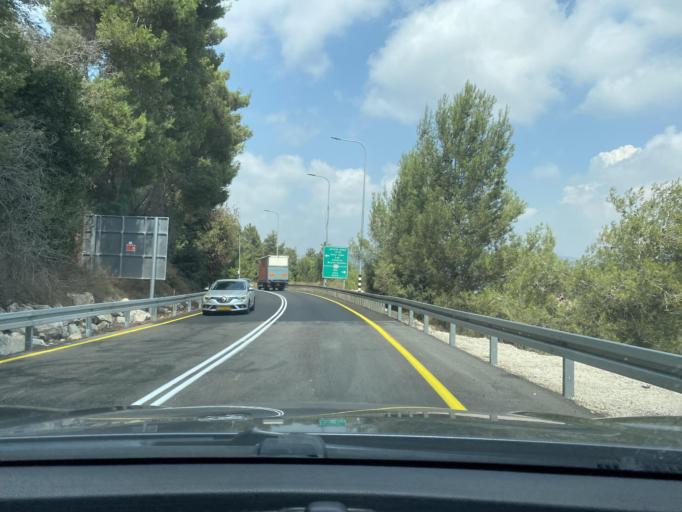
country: IL
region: Northern District
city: Kefar Weradim
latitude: 33.0028
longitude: 35.2836
